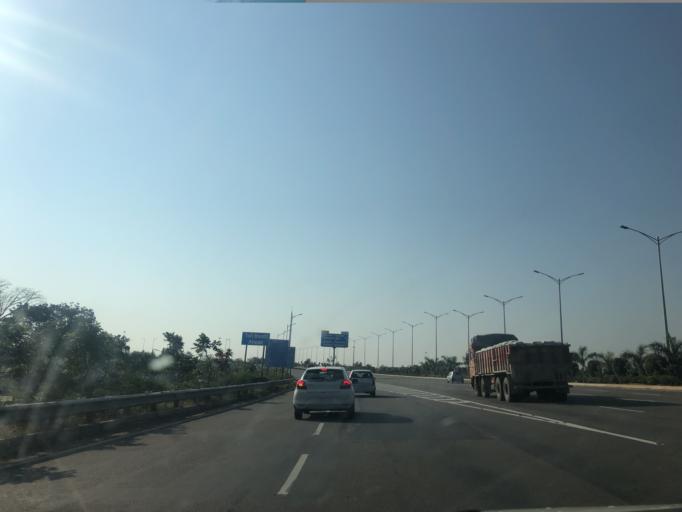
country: IN
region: Telangana
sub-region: Rangareddi
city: Sriramnagar
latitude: 17.2562
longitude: 78.3758
